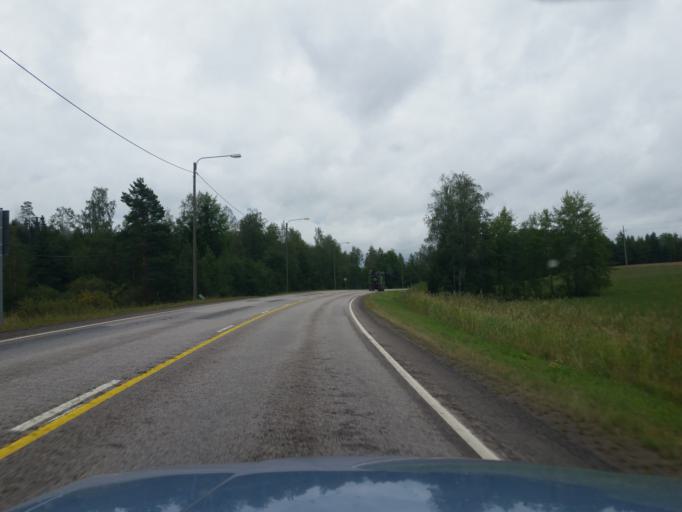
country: FI
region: Uusimaa
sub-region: Helsinki
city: Lohja
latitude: 60.3687
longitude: 24.1565
